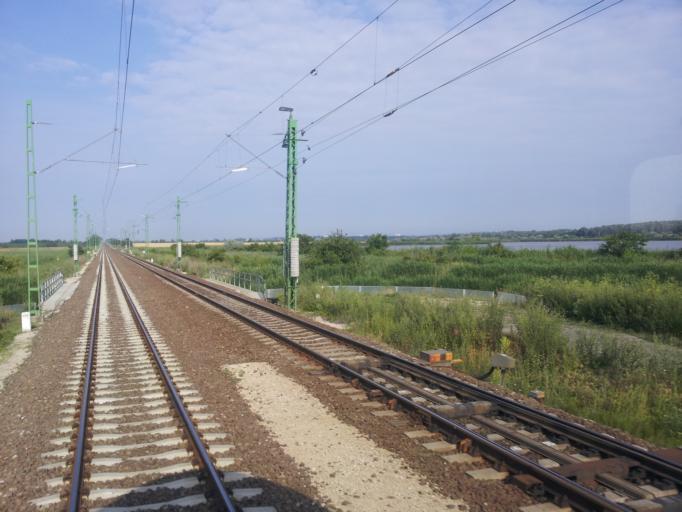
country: HU
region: Fejer
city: Pakozd
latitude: 47.1759
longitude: 18.5378
